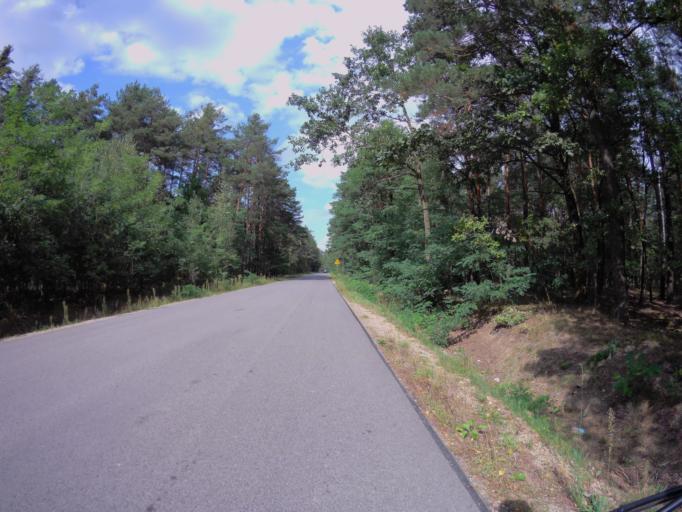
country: PL
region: Subcarpathian Voivodeship
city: Nowa Sarzyna
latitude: 50.2772
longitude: 22.3525
